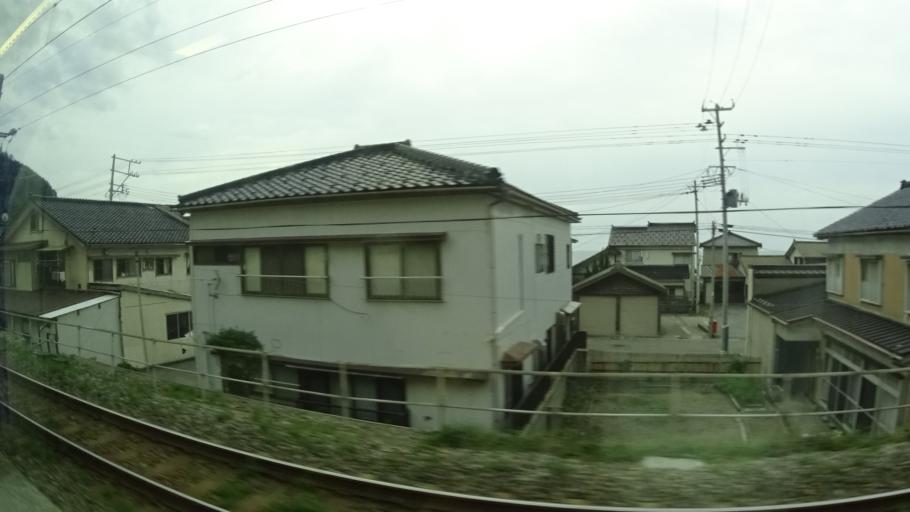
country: JP
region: Yamagata
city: Tsuruoka
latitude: 38.6229
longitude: 139.5871
